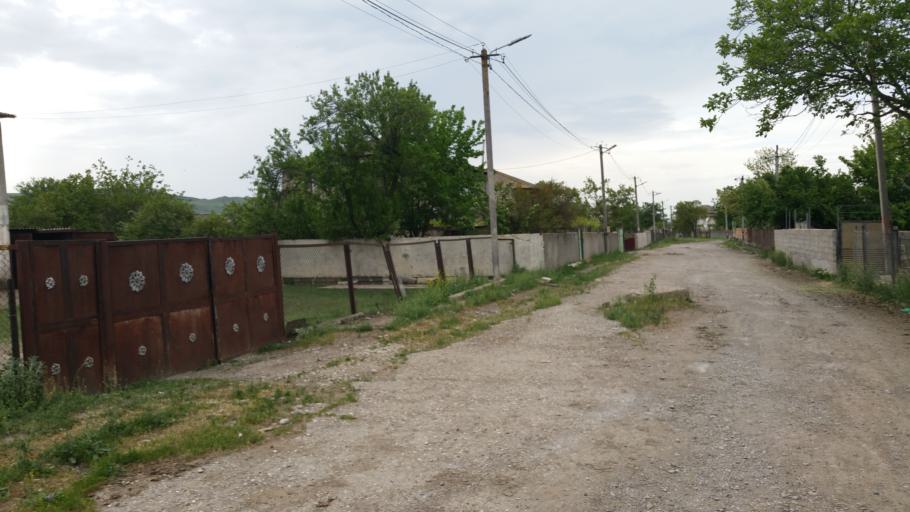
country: AZ
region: Agstafa
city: Saloglu
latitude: 41.5030
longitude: 45.3777
